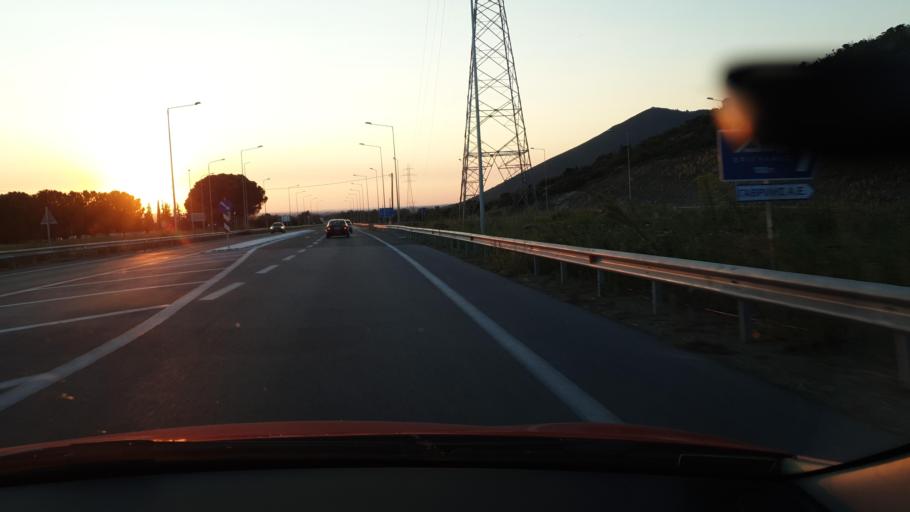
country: GR
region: Central Macedonia
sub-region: Nomos Thessalonikis
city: Vasilika
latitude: 40.4662
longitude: 23.1982
